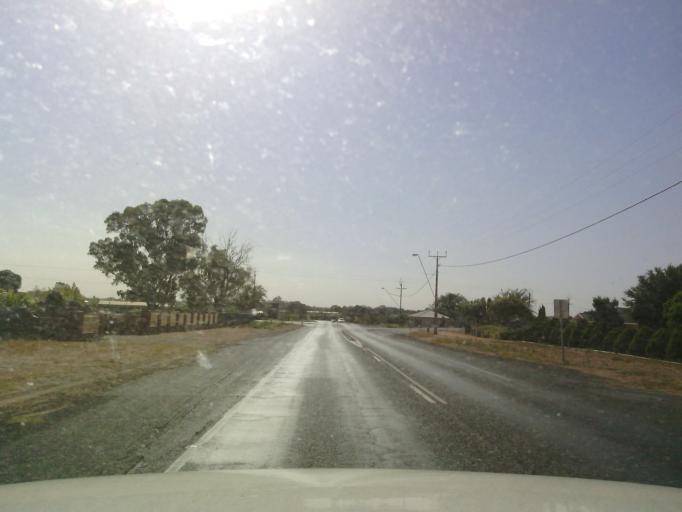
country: AU
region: South Australia
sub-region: Berri and Barmera
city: Berri
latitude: -34.2817
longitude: 140.5819
